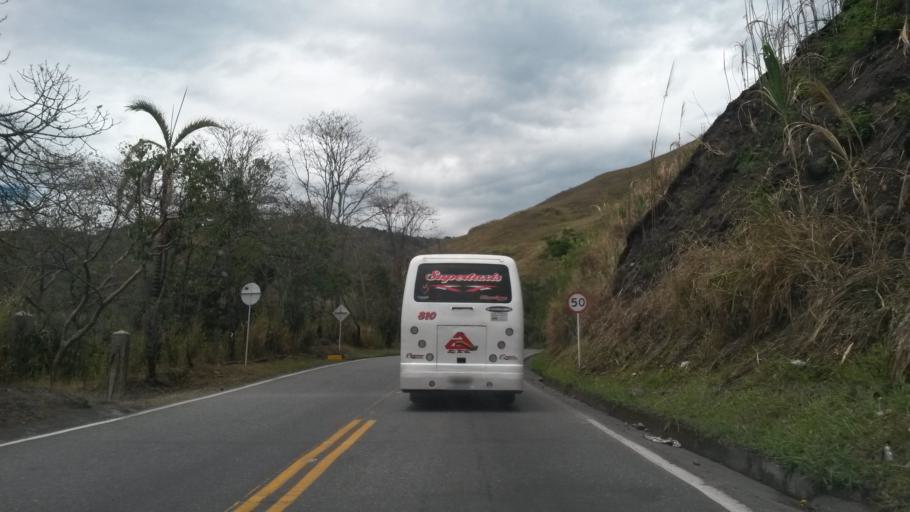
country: CO
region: Cauca
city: Rosas
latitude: 2.2760
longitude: -76.7091
